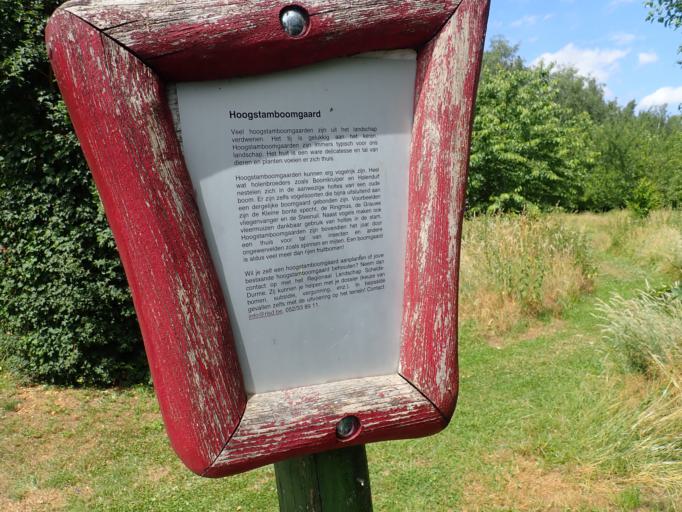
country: BE
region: Flanders
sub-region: Provincie Oost-Vlaanderen
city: Hamme
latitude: 51.0940
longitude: 4.1385
